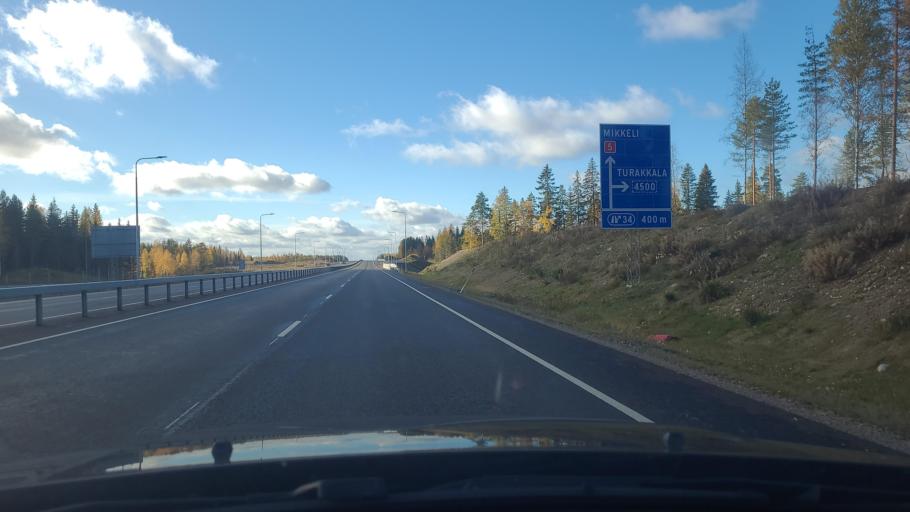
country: FI
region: Southern Savonia
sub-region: Pieksaemaeki
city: Juva
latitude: 61.8612
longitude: 27.7213
